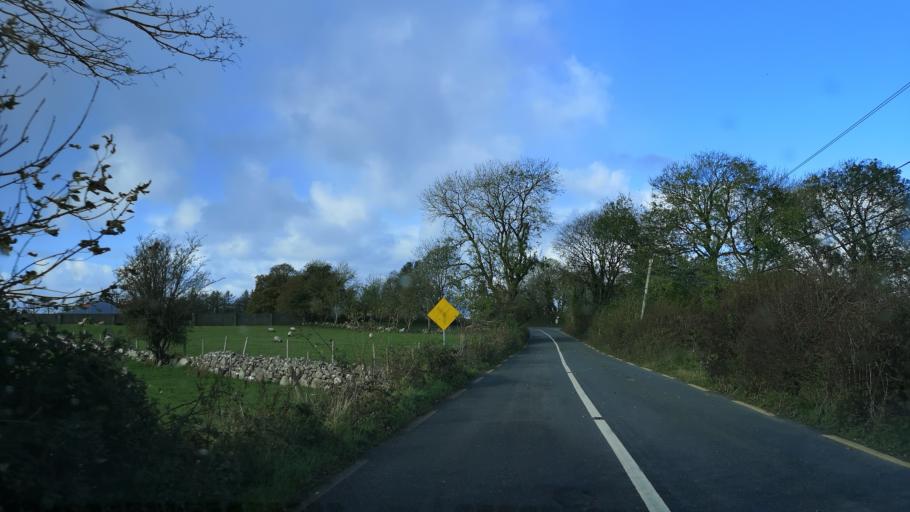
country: IE
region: Connaught
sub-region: Maigh Eo
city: Westport
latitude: 53.7758
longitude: -9.4014
